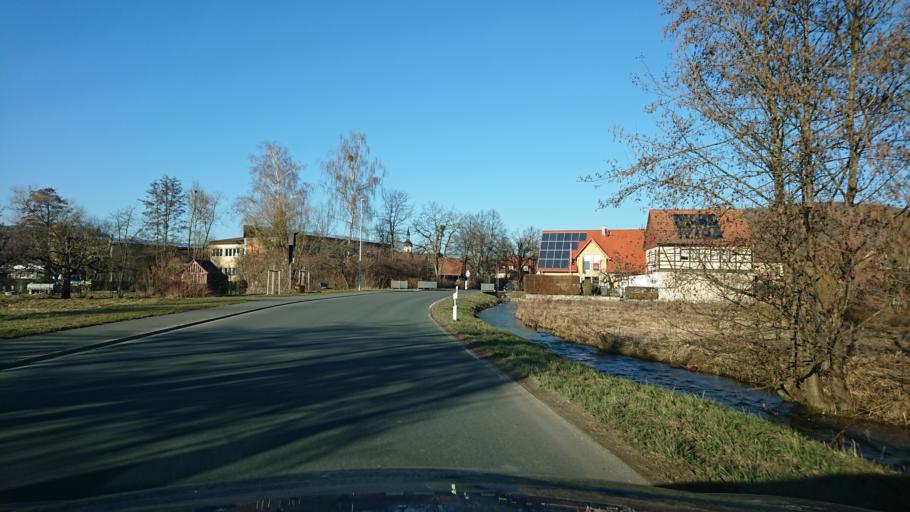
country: DE
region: Bavaria
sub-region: Upper Franconia
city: Pretzfeld
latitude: 49.7526
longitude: 11.1709
